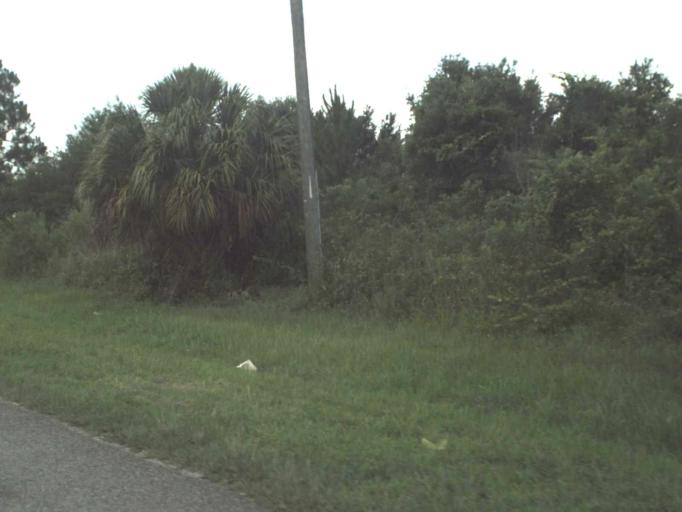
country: US
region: Florida
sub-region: Sumter County
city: Wildwood
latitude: 28.8340
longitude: -82.0455
